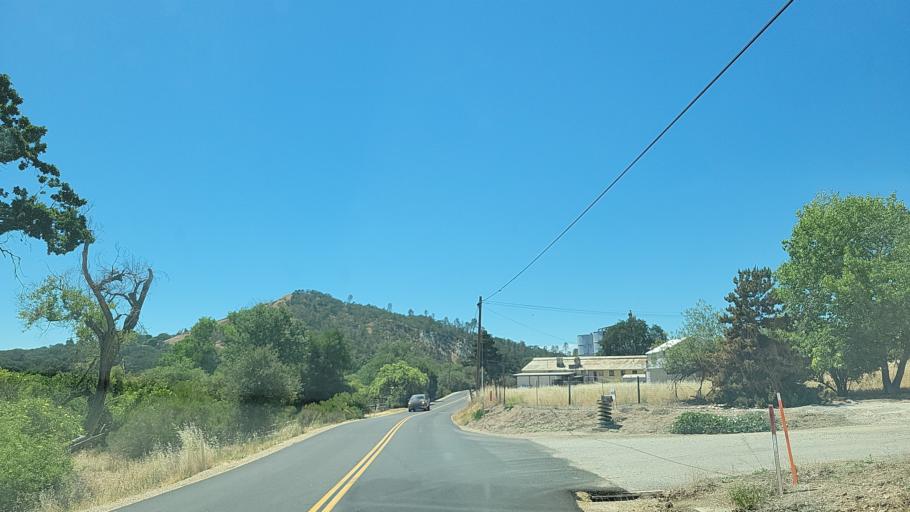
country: US
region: California
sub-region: San Luis Obispo County
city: Atascadero
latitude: 35.4910
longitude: -120.6415
